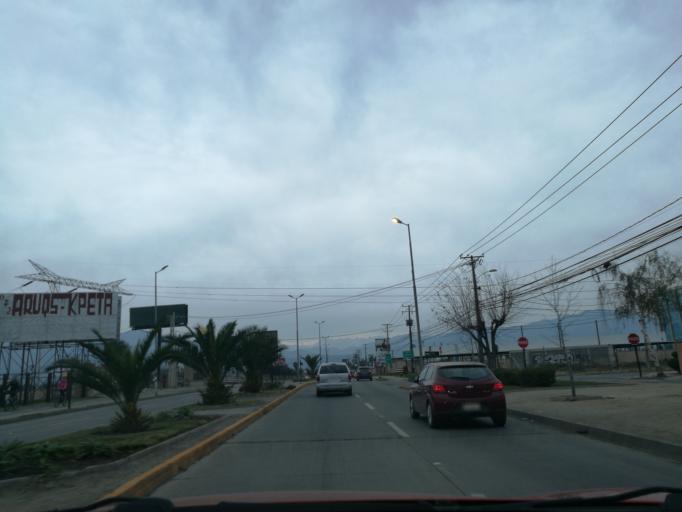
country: CL
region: O'Higgins
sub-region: Provincia de Cachapoal
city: Rancagua
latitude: -34.1756
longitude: -70.7020
